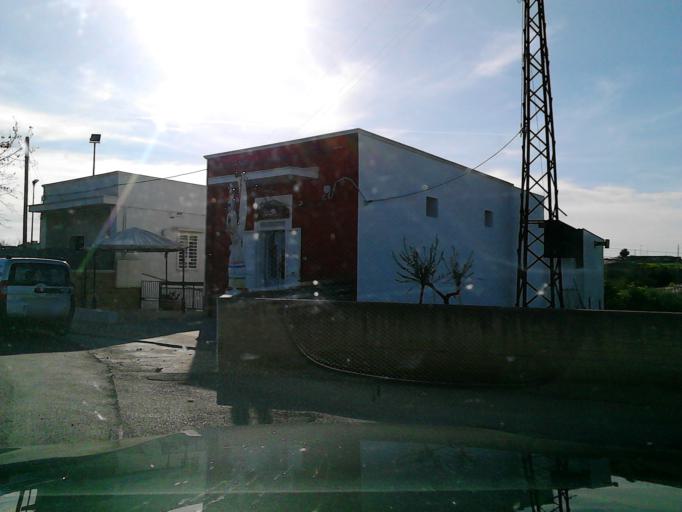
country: IT
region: Apulia
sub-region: Provincia di Bari
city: Rutigliano
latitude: 41.0189
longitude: 16.9988
